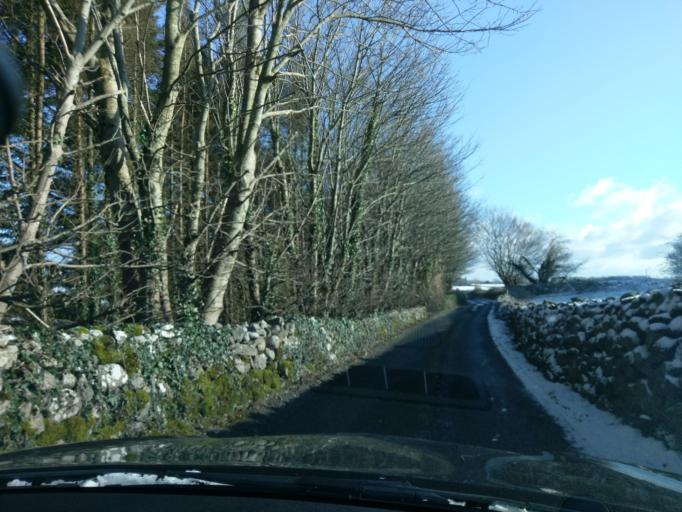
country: IE
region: Connaught
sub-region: County Galway
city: Athenry
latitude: 53.1959
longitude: -8.7965
